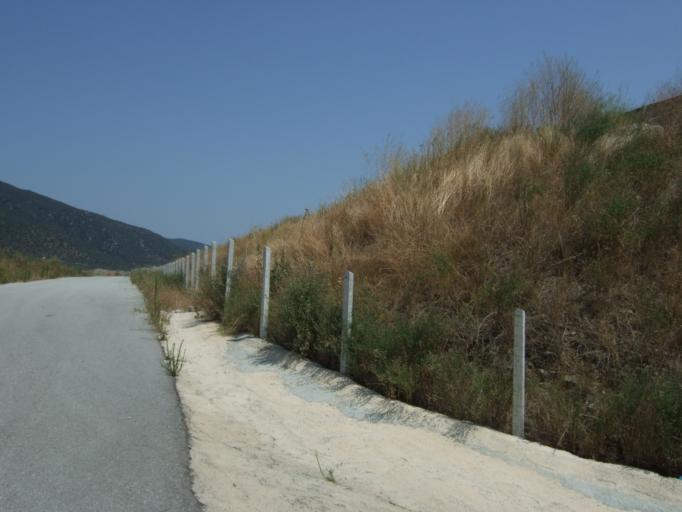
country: GR
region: Central Macedonia
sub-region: Nomos Thessalonikis
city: Nea Apollonia
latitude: 40.6936
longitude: 23.5026
